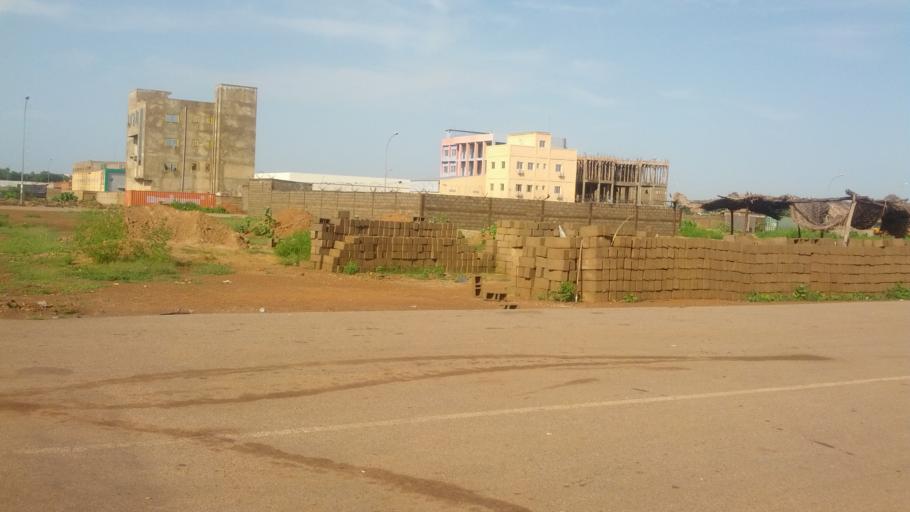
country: BF
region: Centre
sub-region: Kadiogo Province
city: Ouagadougou
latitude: 12.3489
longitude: -1.4926
